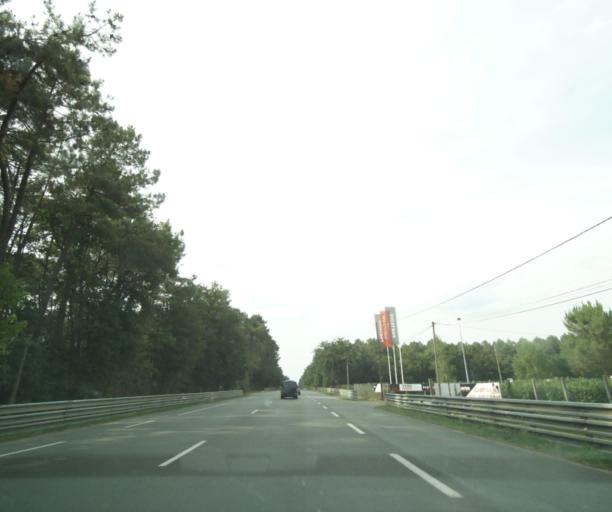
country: FR
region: Pays de la Loire
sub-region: Departement de la Sarthe
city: Mulsanne
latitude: 47.9331
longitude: 0.2390
